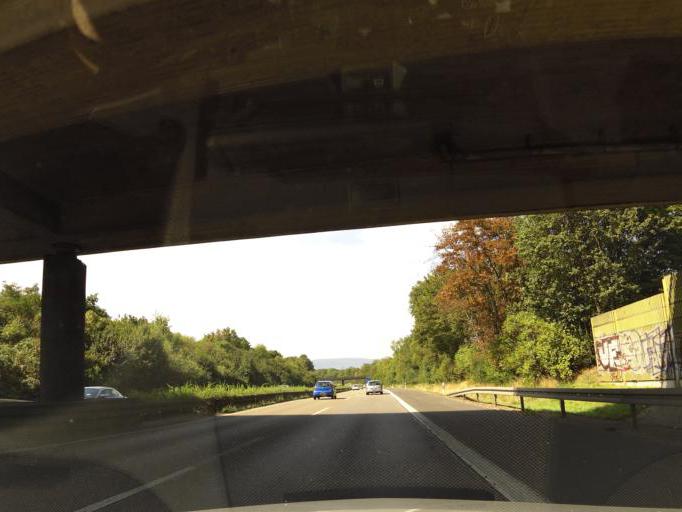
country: DE
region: Hesse
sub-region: Regierungsbezirk Darmstadt
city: Frankfurt am Main
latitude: 50.1649
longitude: 8.6665
